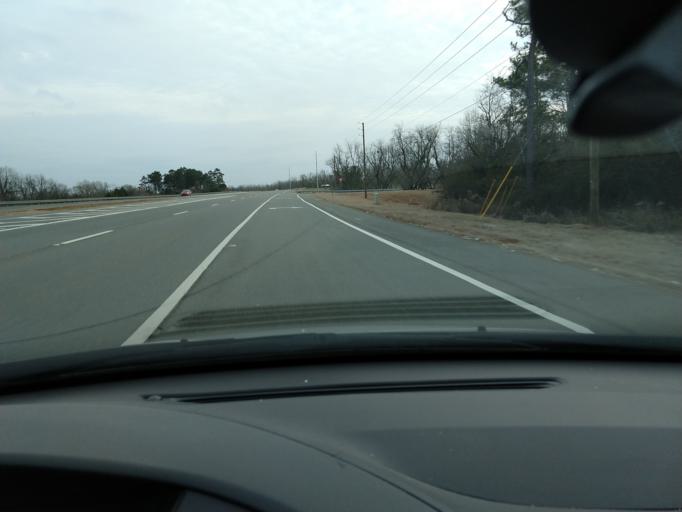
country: US
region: Georgia
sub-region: Sumter County
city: Americus
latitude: 32.0476
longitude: -84.2543
